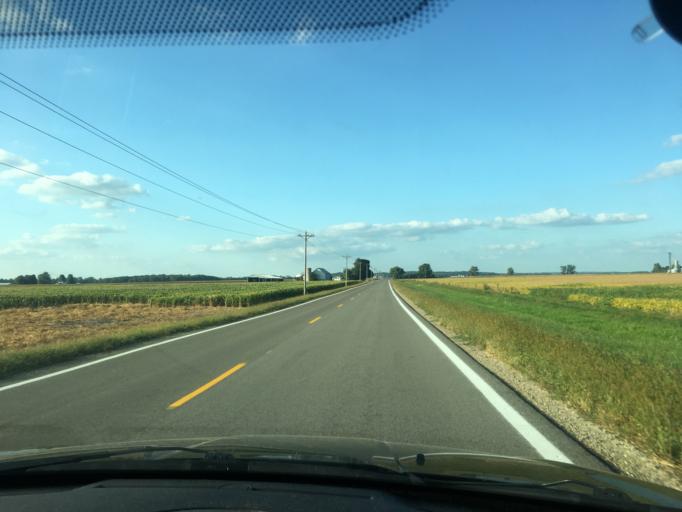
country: US
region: Ohio
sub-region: Logan County
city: West Liberty
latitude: 40.1862
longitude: -83.7816
